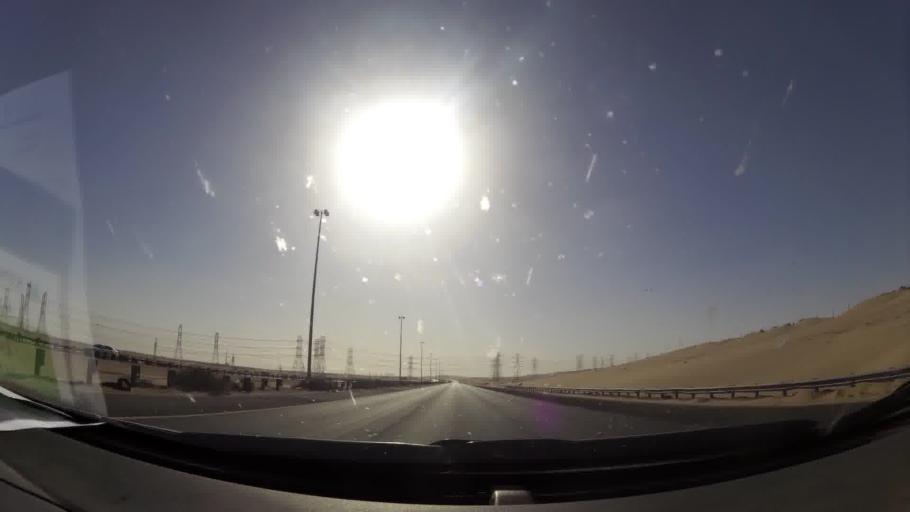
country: KW
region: Al Asimah
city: Kuwait City
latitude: 29.6313
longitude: 47.9294
